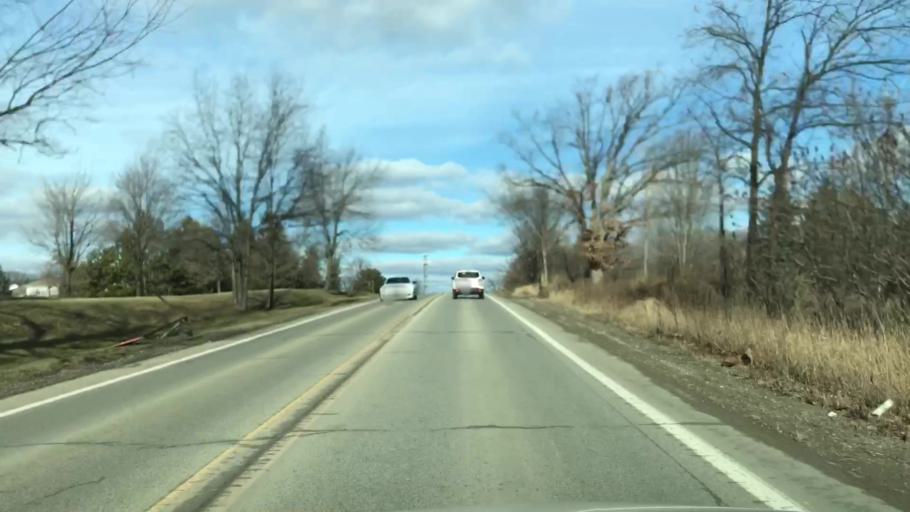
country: US
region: Michigan
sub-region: Oakland County
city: Auburn Hills
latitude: 42.7275
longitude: -83.1964
